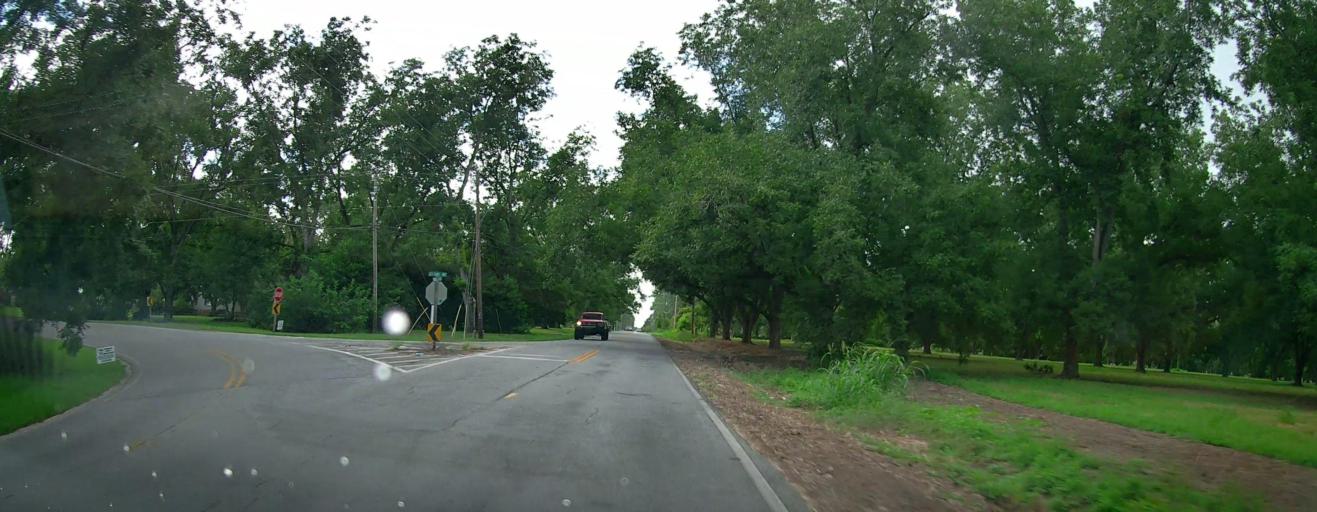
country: US
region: Georgia
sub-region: Ben Hill County
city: Fitzgerald
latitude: 31.7054
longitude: -83.2773
